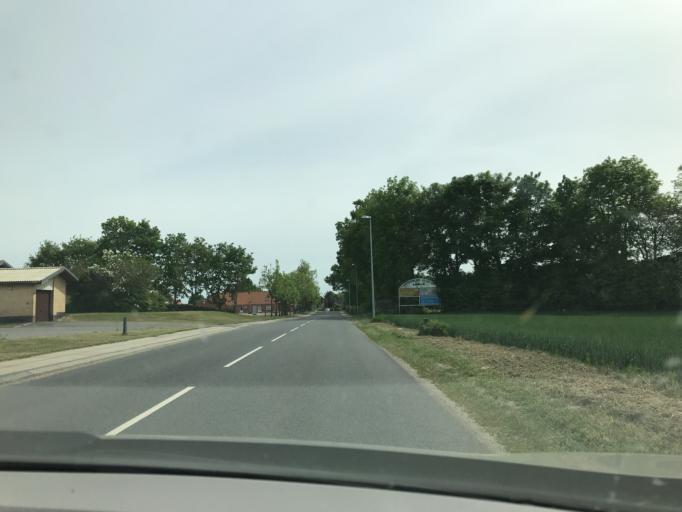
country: DK
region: Central Jutland
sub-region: Norddjurs Kommune
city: Allingabro
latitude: 56.5084
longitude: 10.3333
